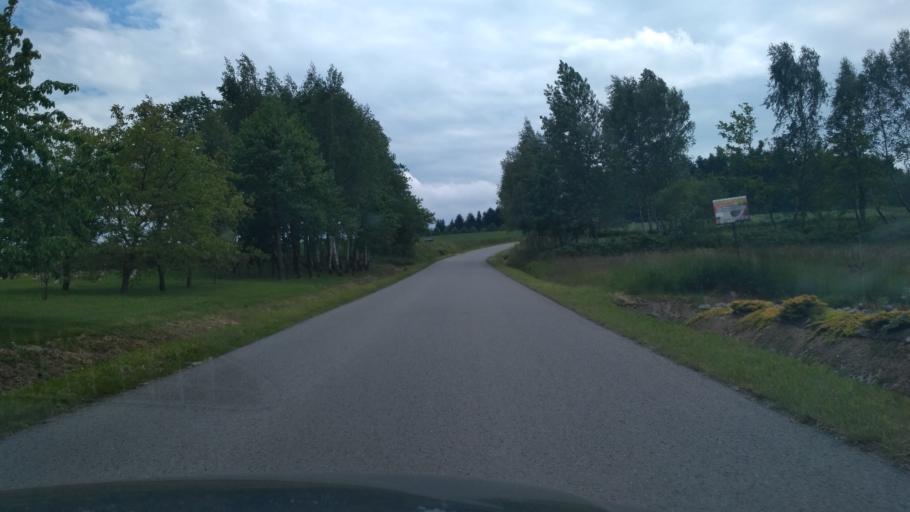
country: PL
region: Subcarpathian Voivodeship
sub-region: Powiat ropczycko-sedziszowski
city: Wielopole Skrzynskie
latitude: 49.9894
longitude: 21.6157
